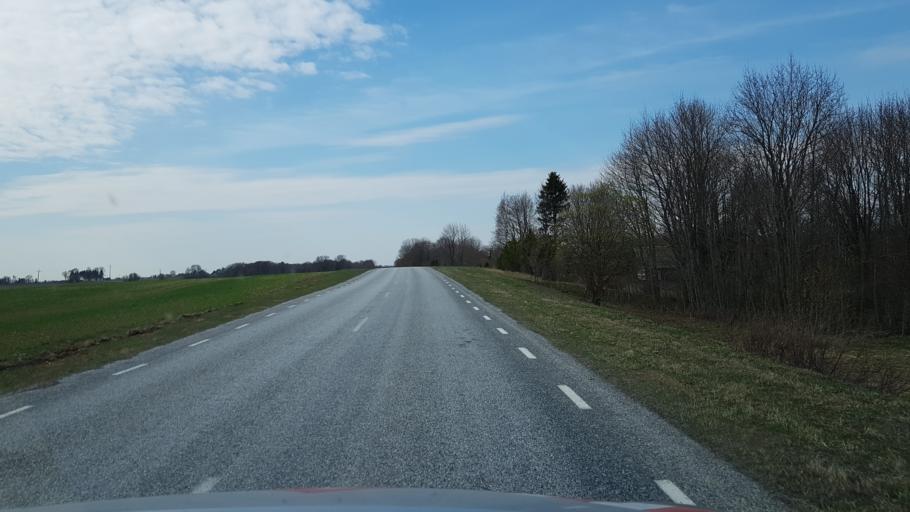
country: EE
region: Laeaene-Virumaa
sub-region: Haljala vald
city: Haljala
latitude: 59.4718
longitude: 26.1724
